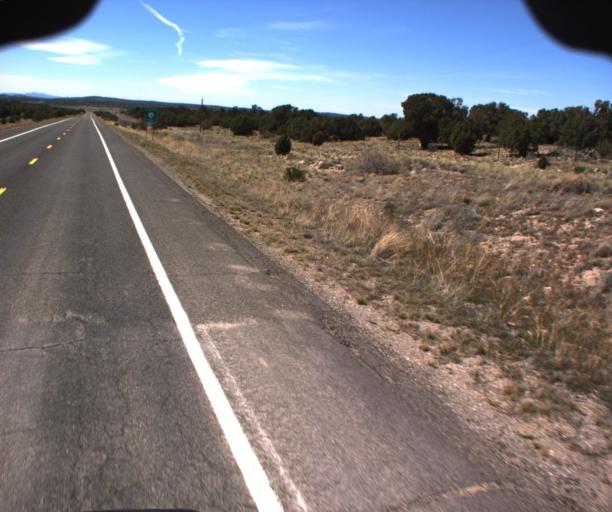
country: US
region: Arizona
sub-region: Mohave County
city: Peach Springs
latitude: 35.5477
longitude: -113.2960
